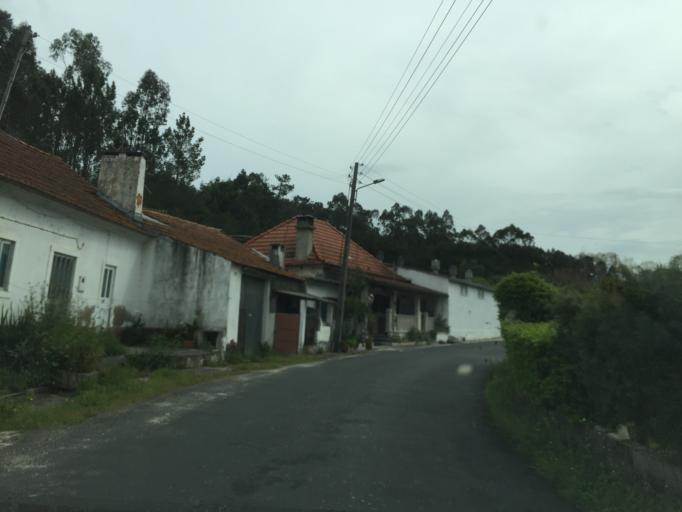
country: PT
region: Leiria
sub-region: Leiria
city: Caranguejeira
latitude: 39.7874
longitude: -8.7312
